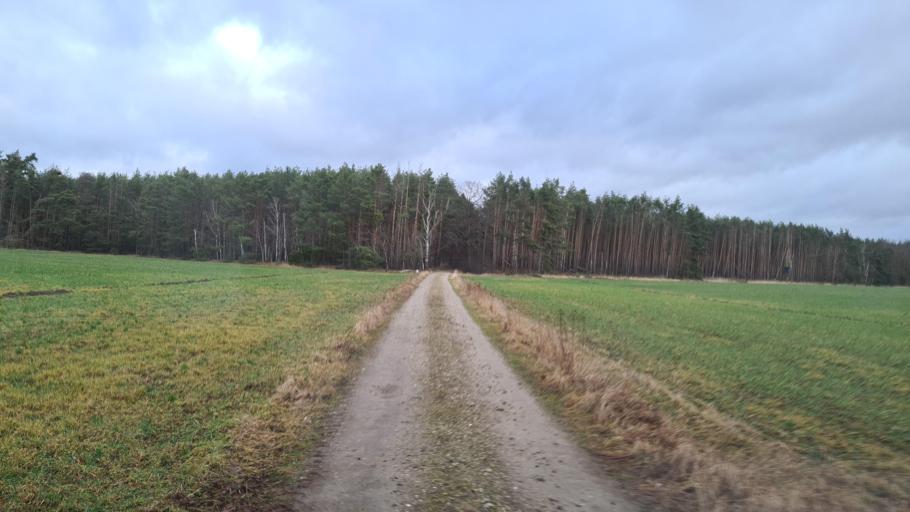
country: DE
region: Brandenburg
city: Ortrand
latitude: 51.3956
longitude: 13.7752
